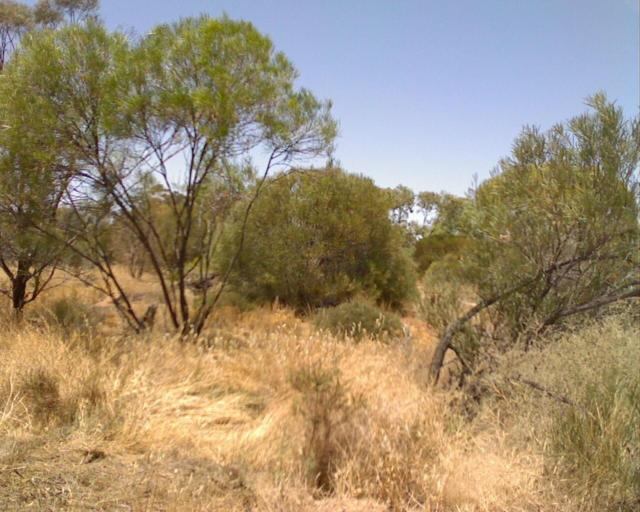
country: AU
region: Western Australia
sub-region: Wongan-Ballidu
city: Wongan Hills
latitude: -30.3606
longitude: 117.1132
